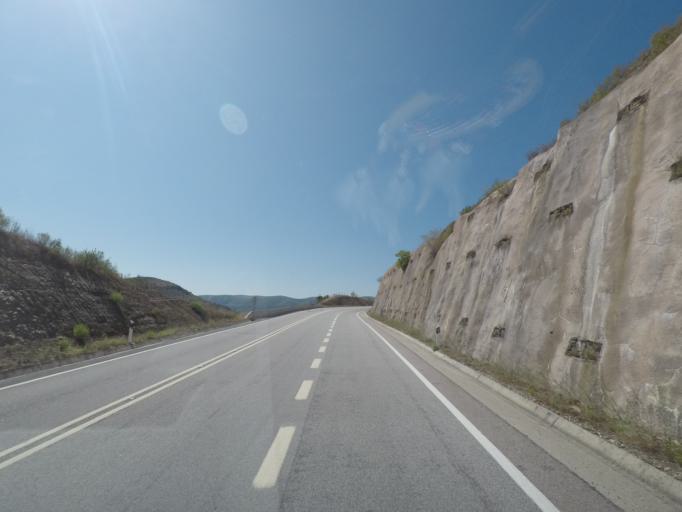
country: PT
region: Braganca
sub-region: Alfandega da Fe
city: Alfandega da Fe
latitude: 41.2850
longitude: -6.8776
